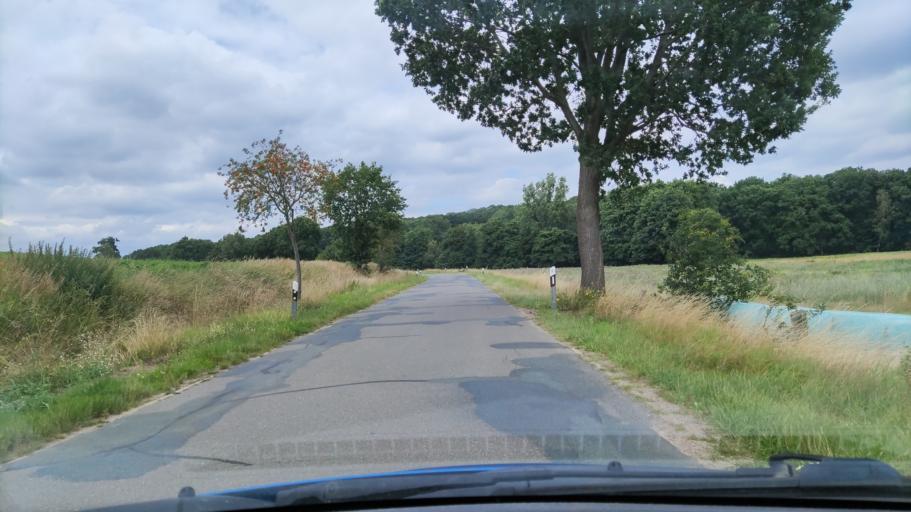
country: DE
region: Lower Saxony
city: Weste
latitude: 53.0776
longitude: 10.6894
